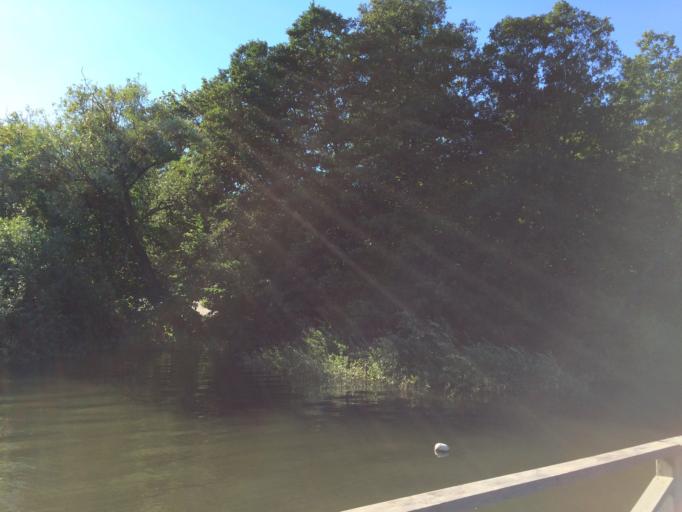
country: SE
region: Stockholm
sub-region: Stockholms Kommun
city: Arsta
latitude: 59.3115
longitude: 18.0098
